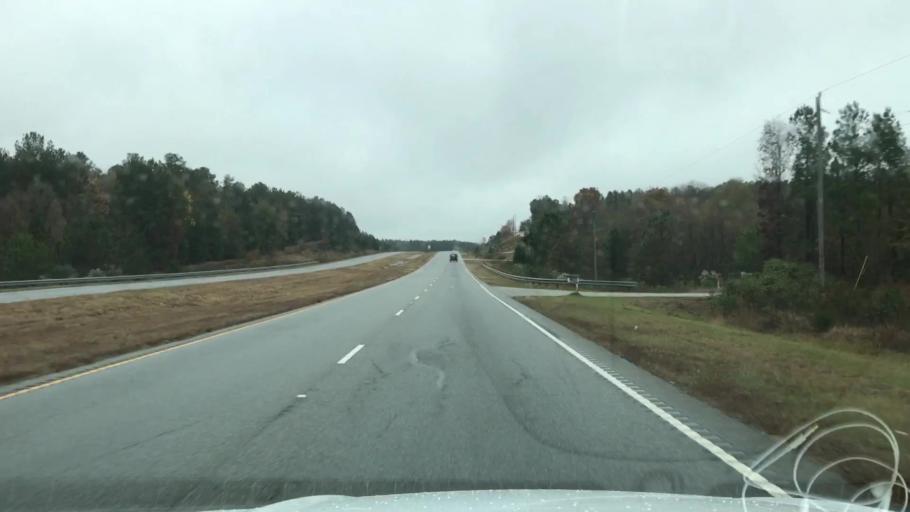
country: US
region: South Carolina
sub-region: Greenwood County
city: Ninety Six
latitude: 34.3302
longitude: -81.9855
